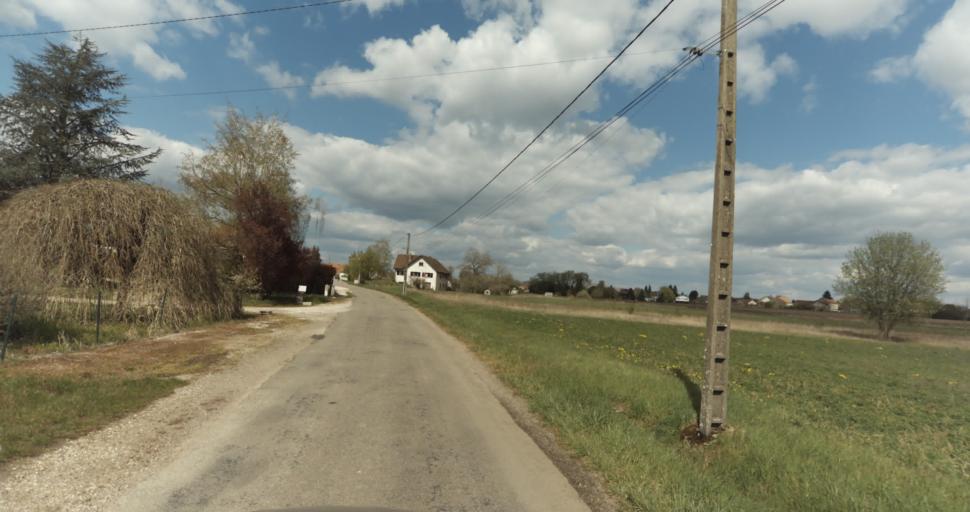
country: FR
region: Bourgogne
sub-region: Departement de la Cote-d'Or
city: Auxonne
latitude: 47.1790
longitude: 5.3931
